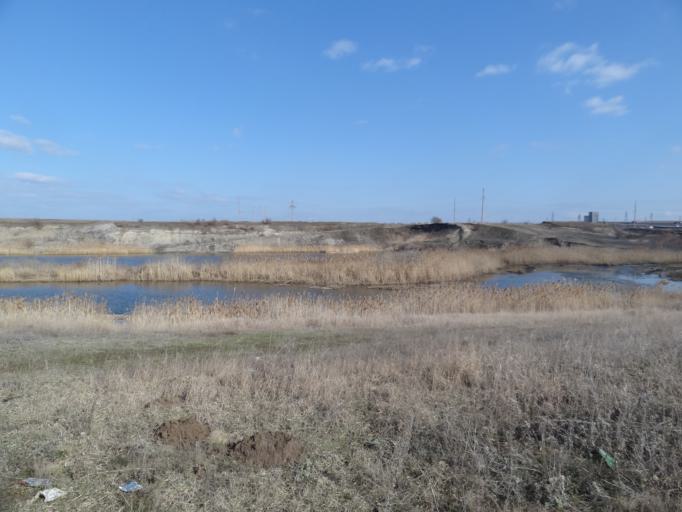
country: RU
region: Saratov
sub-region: Saratovskiy Rayon
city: Saratov
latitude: 51.6728
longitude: 46.0191
